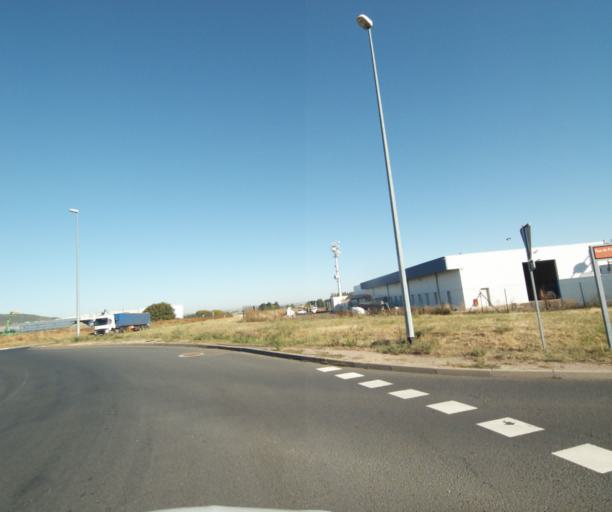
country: FR
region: Auvergne
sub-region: Departement du Puy-de-Dome
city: Gerzat
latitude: 45.8343
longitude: 3.1391
